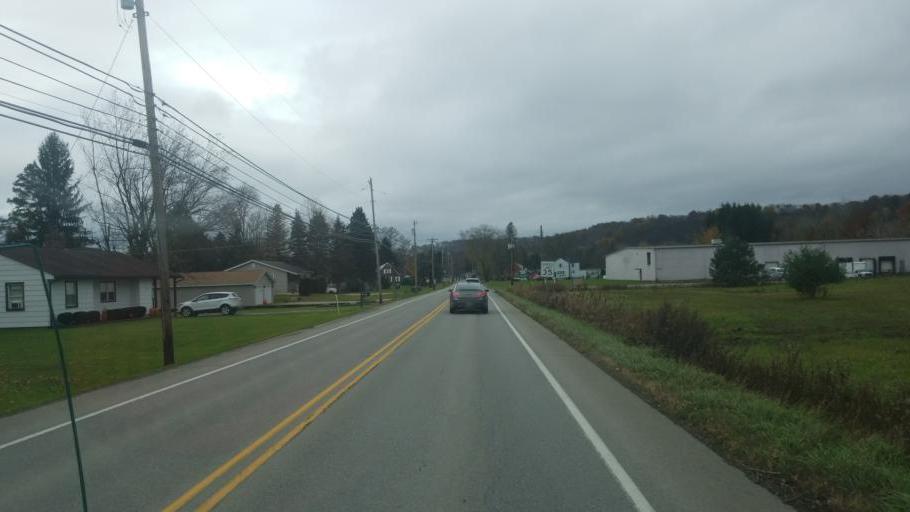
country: US
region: Pennsylvania
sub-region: Jefferson County
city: Brockway
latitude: 41.2558
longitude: -78.7323
